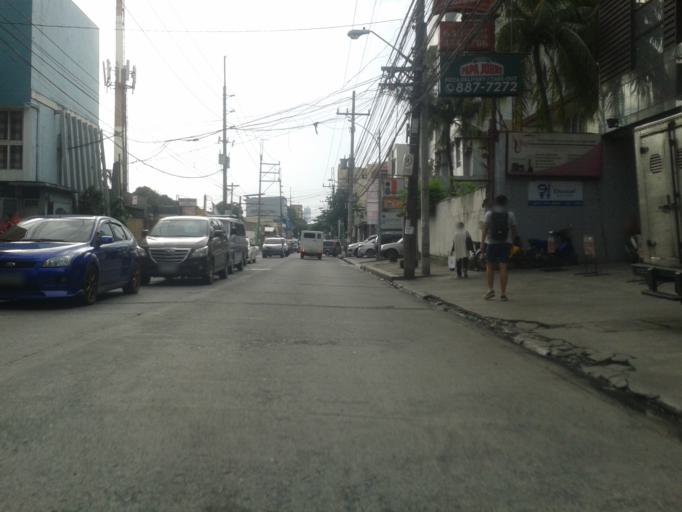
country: PH
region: Metro Manila
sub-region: Marikina
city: Calumpang
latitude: 14.6342
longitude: 121.0725
